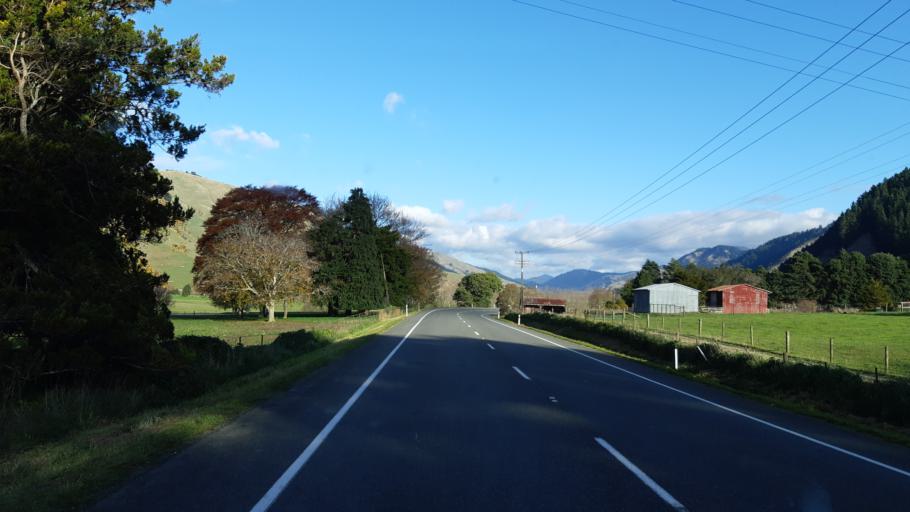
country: NZ
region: Marlborough
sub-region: Marlborough District
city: Picton
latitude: -41.3016
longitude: 173.7704
